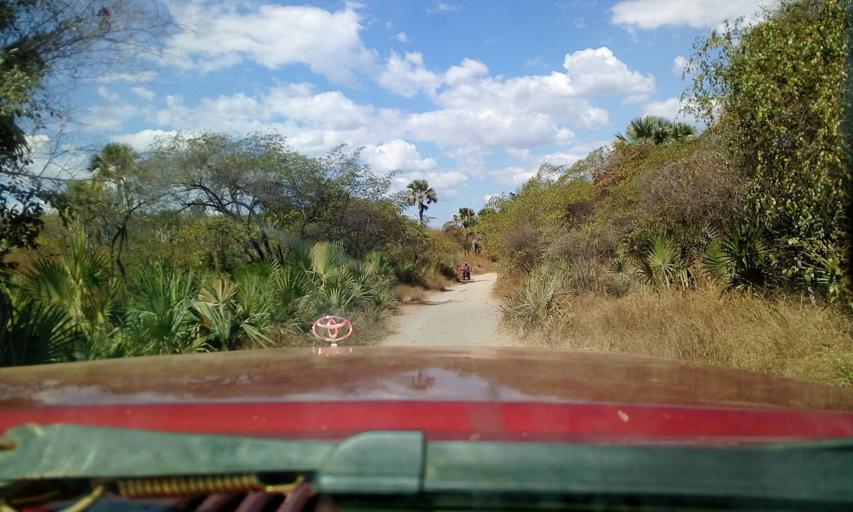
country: MG
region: Boeny
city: Sitampiky
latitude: -16.1287
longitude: 45.4946
